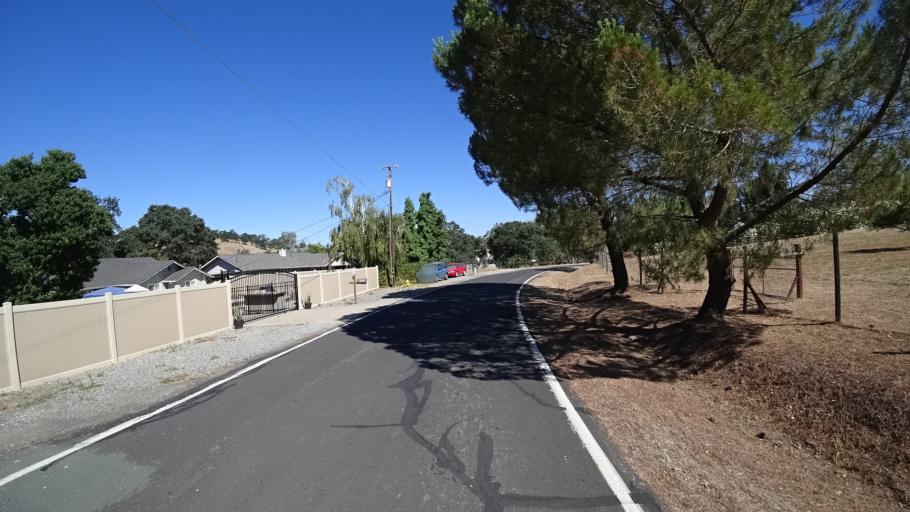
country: US
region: California
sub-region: Calaveras County
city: Rancho Calaveras
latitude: 38.1034
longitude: -120.8771
